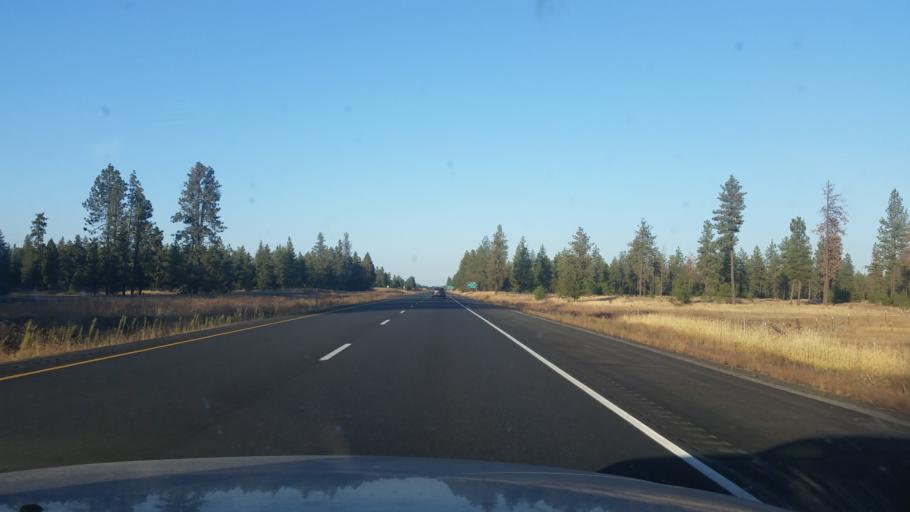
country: US
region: Washington
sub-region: Spokane County
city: Medical Lake
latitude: 47.4945
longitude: -117.7049
